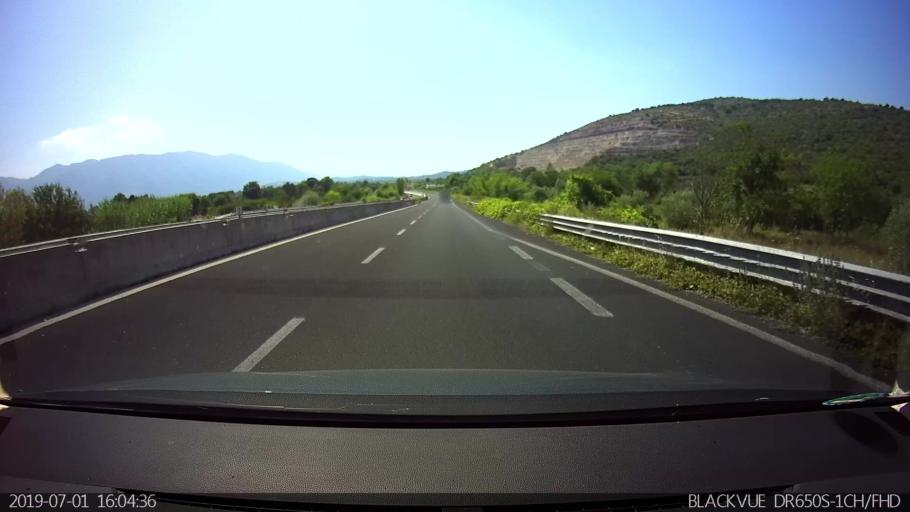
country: IT
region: Latium
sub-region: Provincia di Frosinone
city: Tecchiena
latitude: 41.6711
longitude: 13.3093
